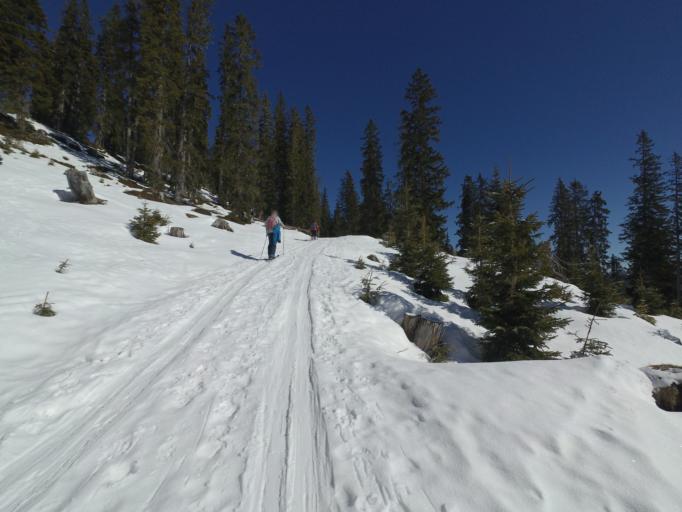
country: AT
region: Salzburg
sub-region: Politischer Bezirk Sankt Johann im Pongau
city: Muhlbach am Hochkonig
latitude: 47.4001
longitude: 13.1354
